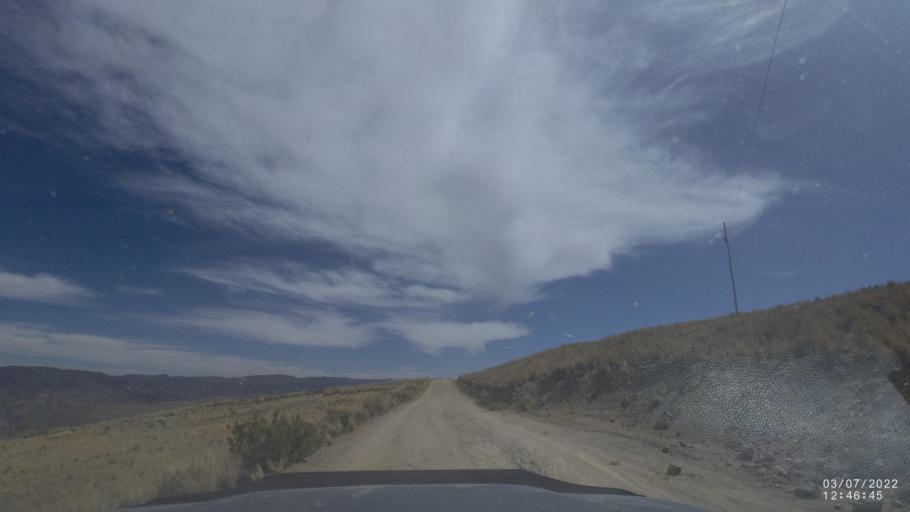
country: BO
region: Cochabamba
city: Irpa Irpa
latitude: -17.7715
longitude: -66.6389
